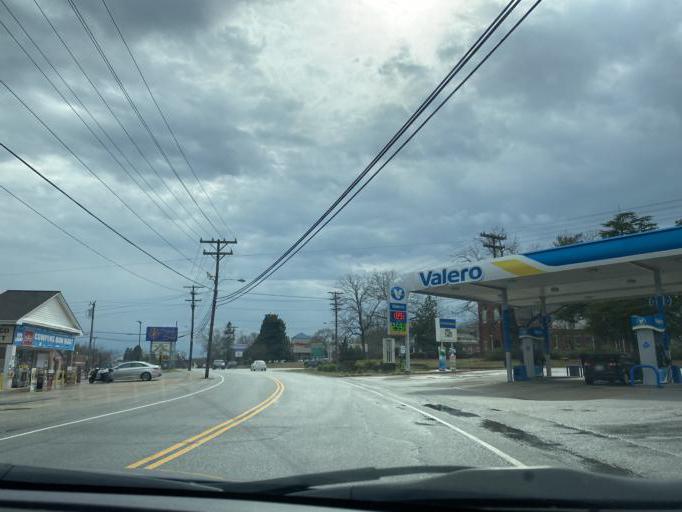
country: US
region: South Carolina
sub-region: Spartanburg County
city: Cowpens
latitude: 35.0208
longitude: -81.8019
